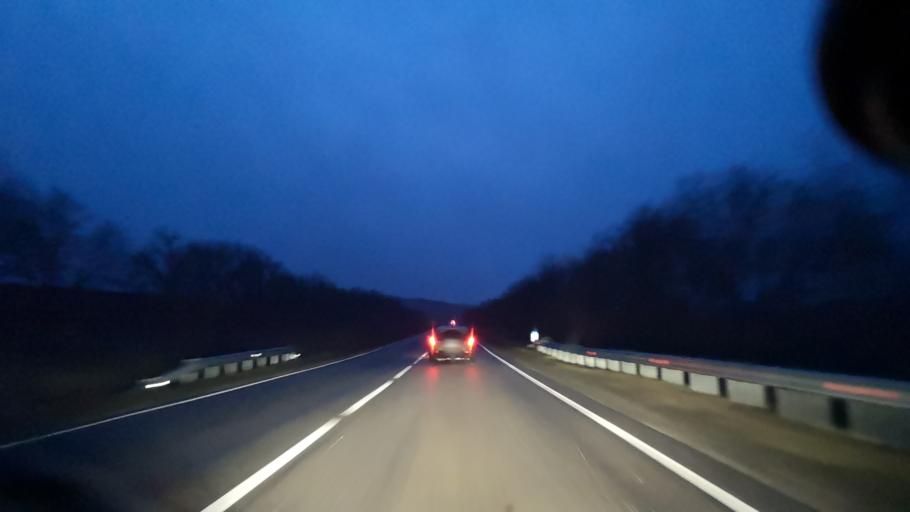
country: MD
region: Orhei
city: Orhei
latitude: 47.4894
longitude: 28.7922
